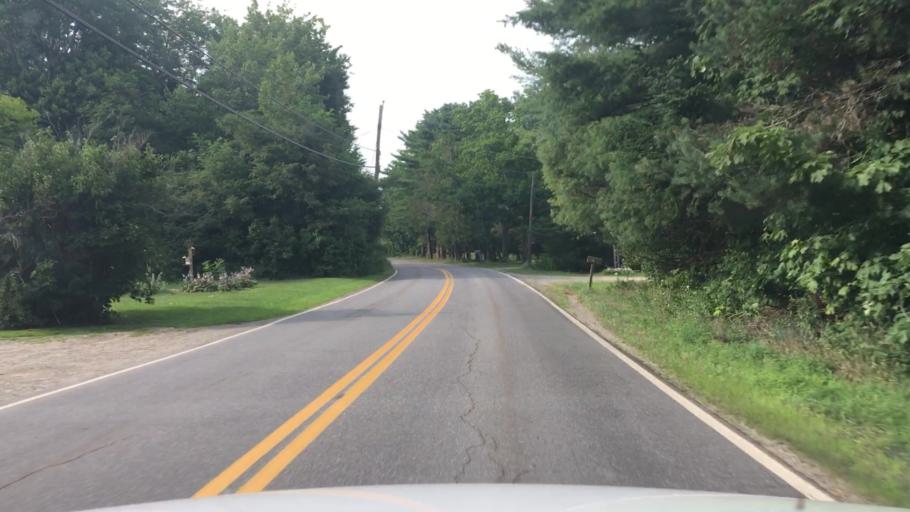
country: US
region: Maine
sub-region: Lincoln County
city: Waldoboro
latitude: 44.1504
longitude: -69.3742
